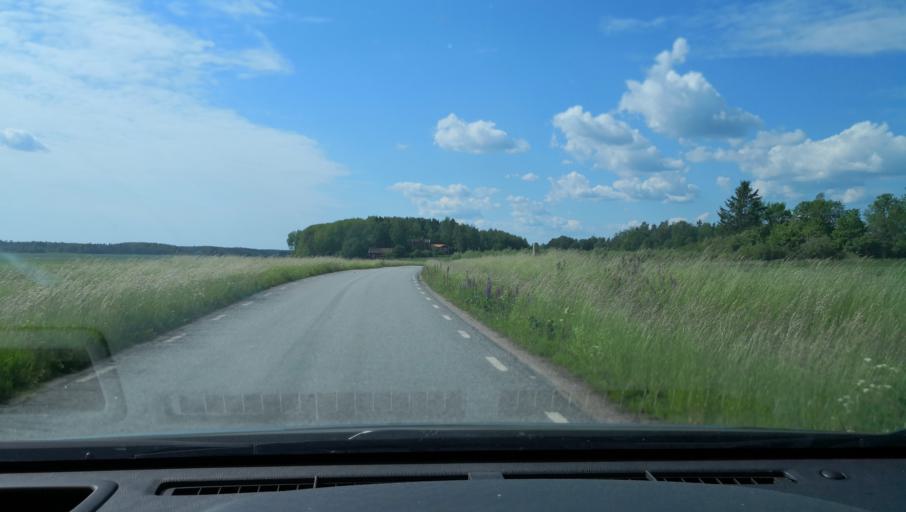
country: SE
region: Uppsala
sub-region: Enkopings Kommun
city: Orsundsbro
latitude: 59.8200
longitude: 17.3289
